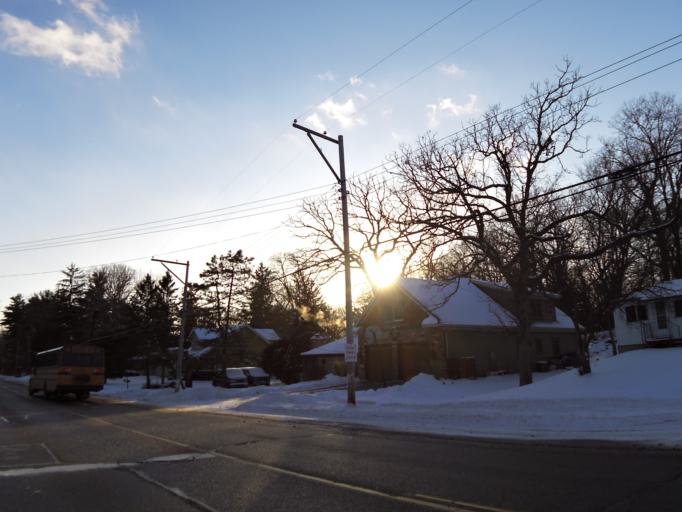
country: US
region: Minnesota
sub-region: Washington County
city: Lake Elmo
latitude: 44.9971
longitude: -92.8793
